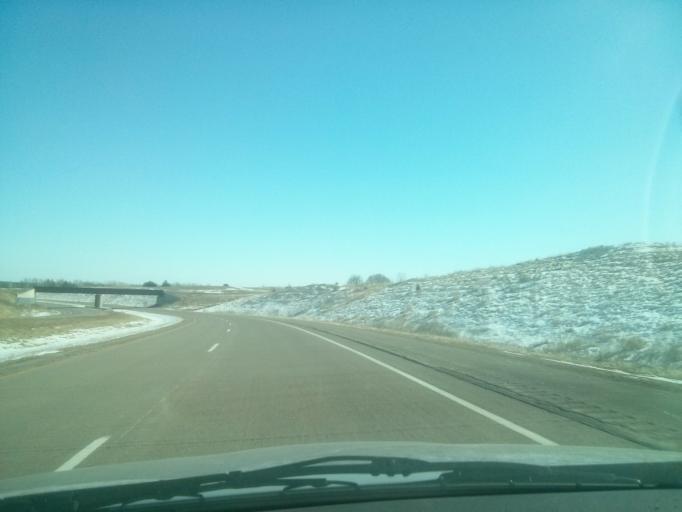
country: US
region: Wisconsin
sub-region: Saint Croix County
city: Somerset
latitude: 45.1096
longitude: -92.6700
